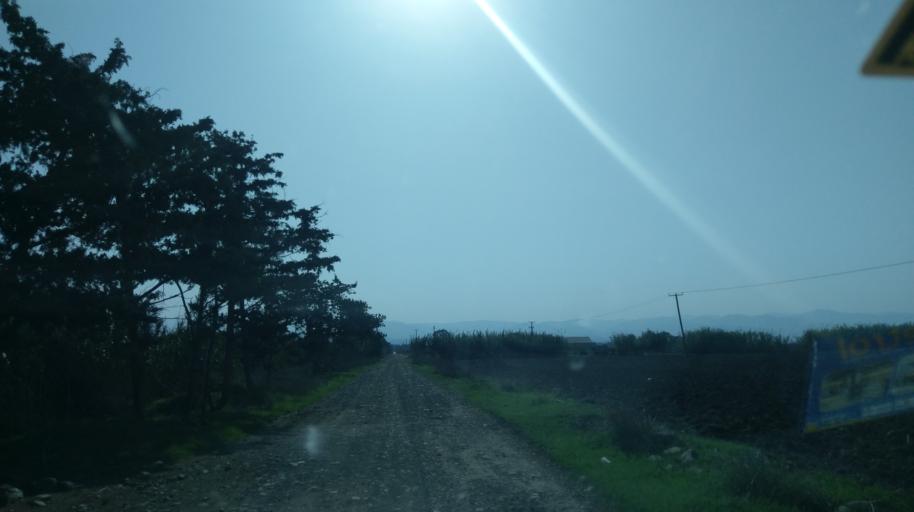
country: CY
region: Lefkosia
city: Morfou
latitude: 35.2018
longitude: 32.9367
